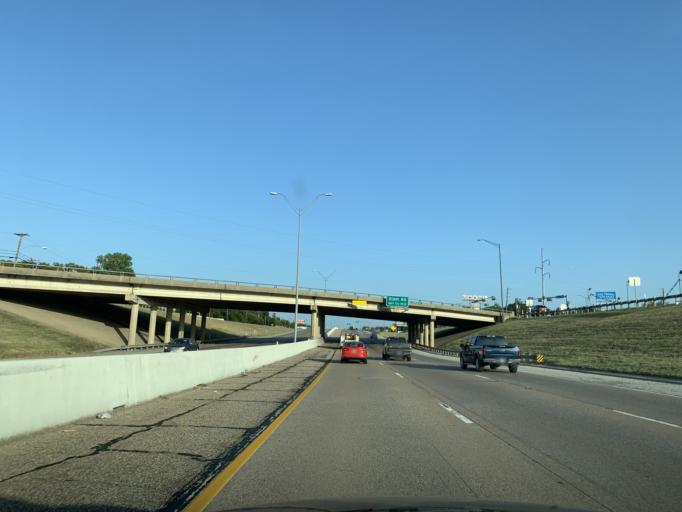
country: US
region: Texas
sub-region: Dallas County
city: Hutchins
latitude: 32.7249
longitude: -96.7011
